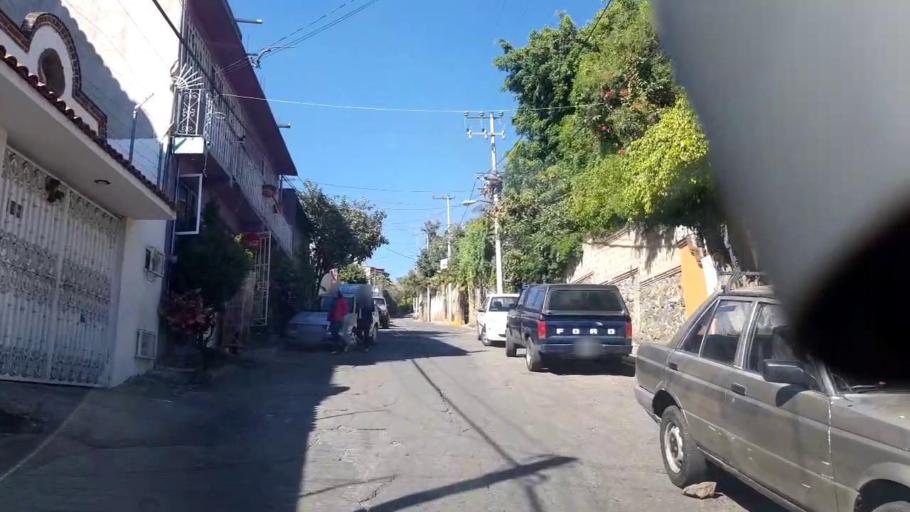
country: MX
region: Morelos
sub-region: Cuernavaca
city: Lomas de Ahuatepec
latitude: 18.9732
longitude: -99.2136
